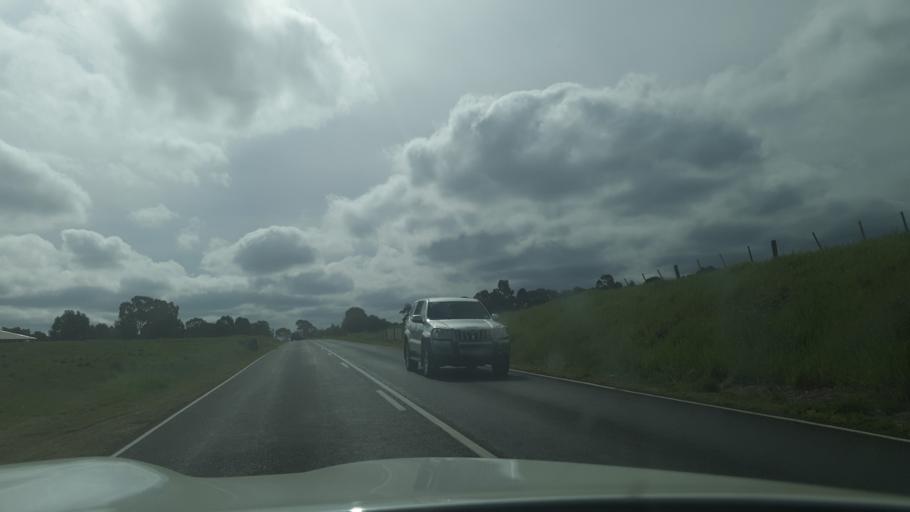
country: AU
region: Victoria
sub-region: Central Goldfields
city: Maryborough
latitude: -37.2116
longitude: 143.7234
